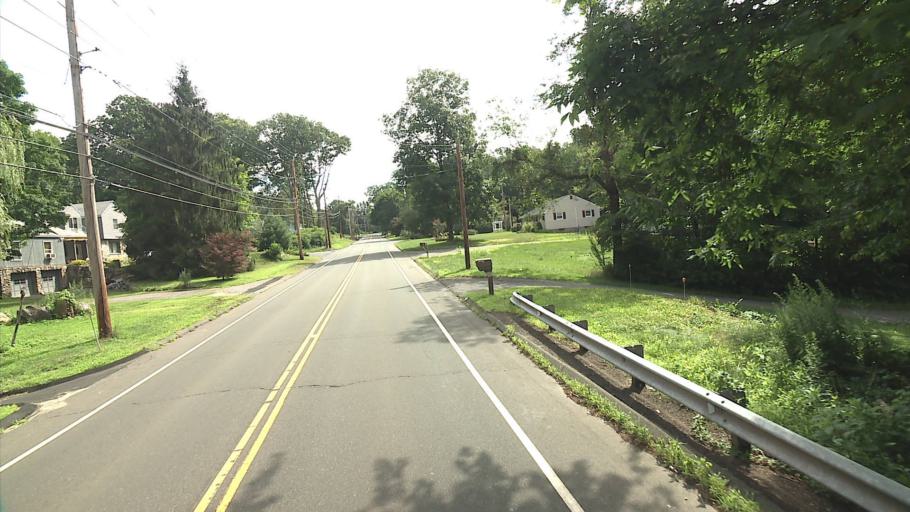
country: US
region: Connecticut
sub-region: New Haven County
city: Ansonia
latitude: 41.3311
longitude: -73.0449
